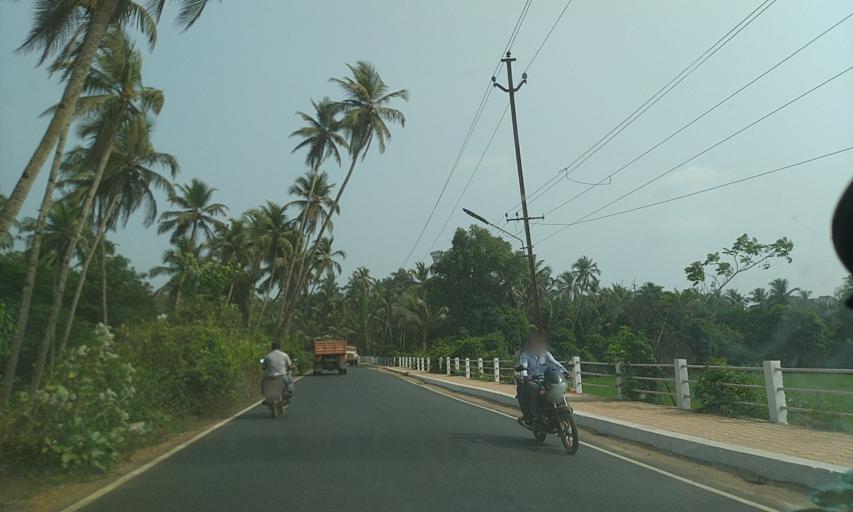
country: IN
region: Goa
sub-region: South Goa
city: Quepem
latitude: 15.2565
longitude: 74.0498
